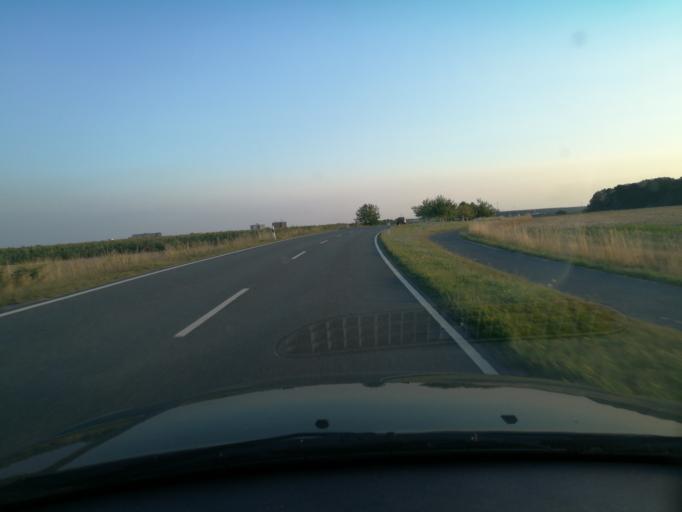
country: DE
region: Bavaria
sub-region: Regierungsbezirk Mittelfranken
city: Herzogenaurach
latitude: 49.5868
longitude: 10.8899
